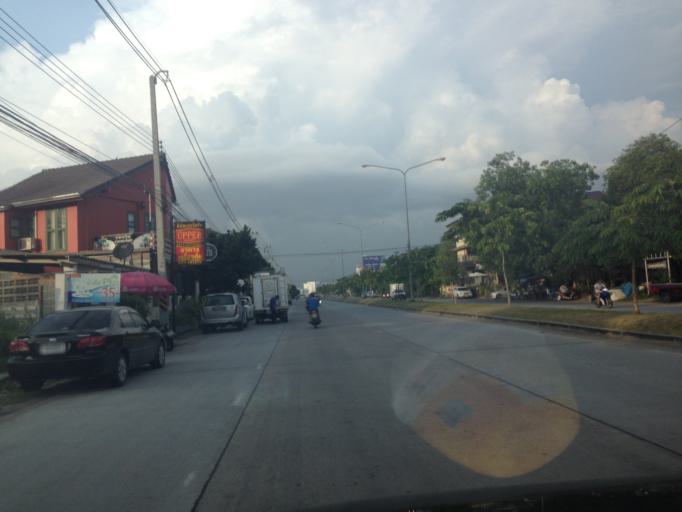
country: TH
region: Chon Buri
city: Chon Buri
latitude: 13.2937
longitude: 100.9162
